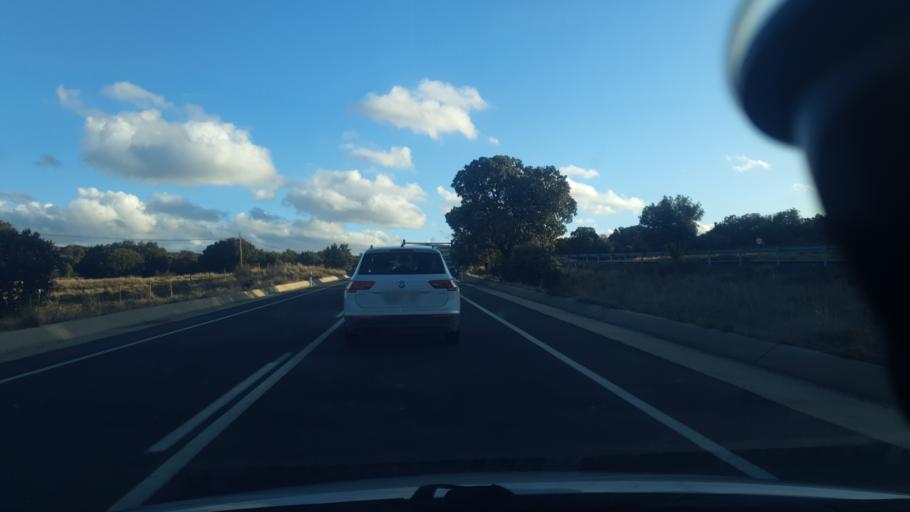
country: ES
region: Castille and Leon
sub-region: Provincia de Avila
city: Mingorria
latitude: 40.7218
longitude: -4.6735
